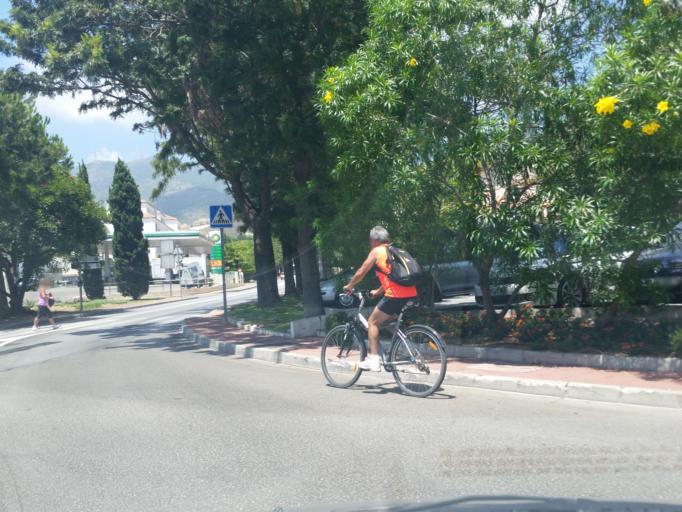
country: ES
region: Andalusia
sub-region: Provincia de Malaga
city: Benalmadena
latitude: 36.6008
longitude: -4.5444
